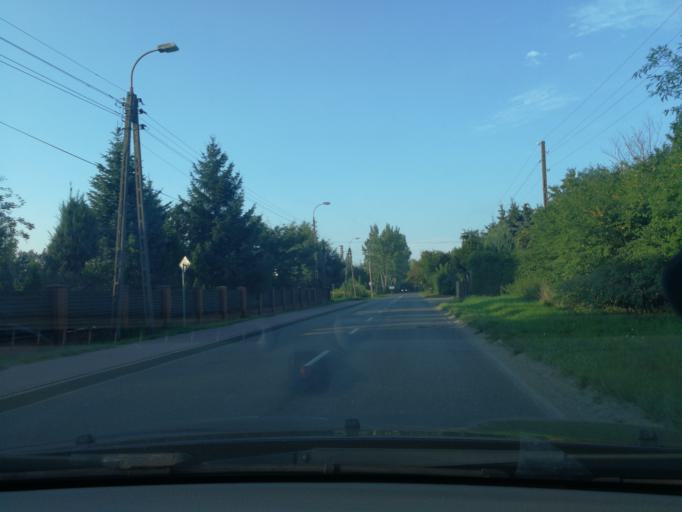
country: PL
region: Masovian Voivodeship
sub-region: Powiat pruszkowski
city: Brwinow
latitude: 52.1521
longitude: 20.7284
